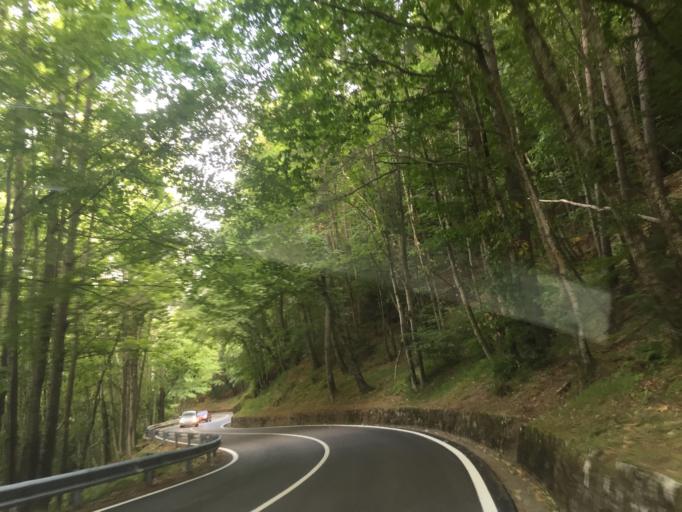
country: IT
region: Tuscany
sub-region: Provincia di Pistoia
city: Cutigliano
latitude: 44.1232
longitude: 10.7231
